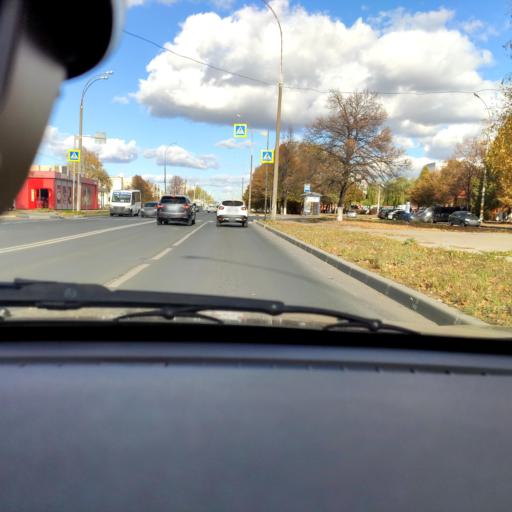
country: RU
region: Samara
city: Tol'yatti
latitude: 53.5327
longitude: 49.3135
